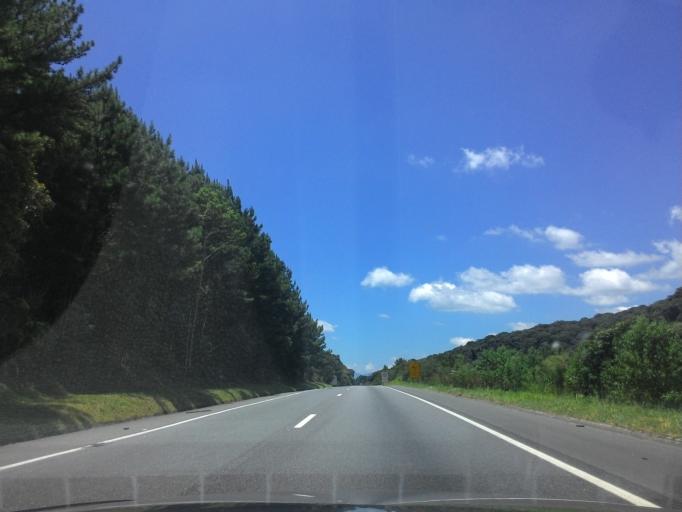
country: BR
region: Sao Paulo
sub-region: Cajati
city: Cajati
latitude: -24.9679
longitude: -48.4402
